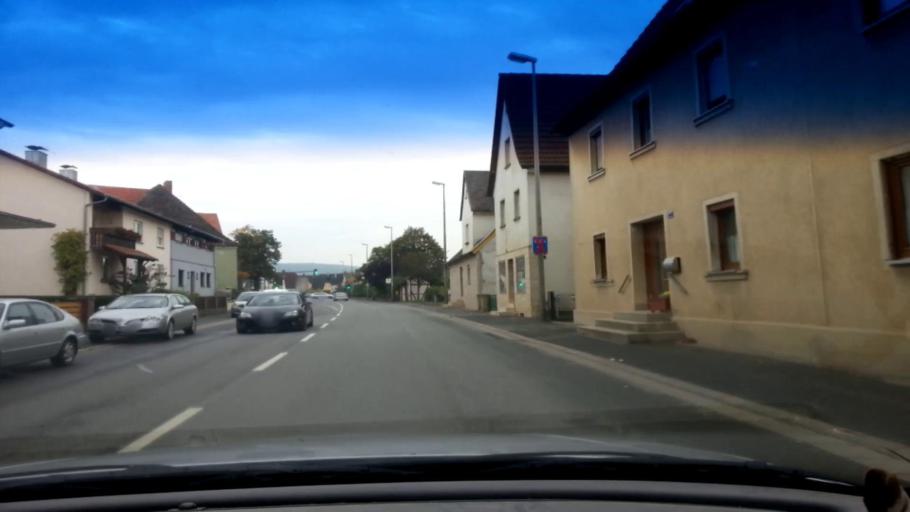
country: DE
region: Bavaria
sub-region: Upper Franconia
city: Zapfendorf
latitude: 50.0184
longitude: 10.9315
